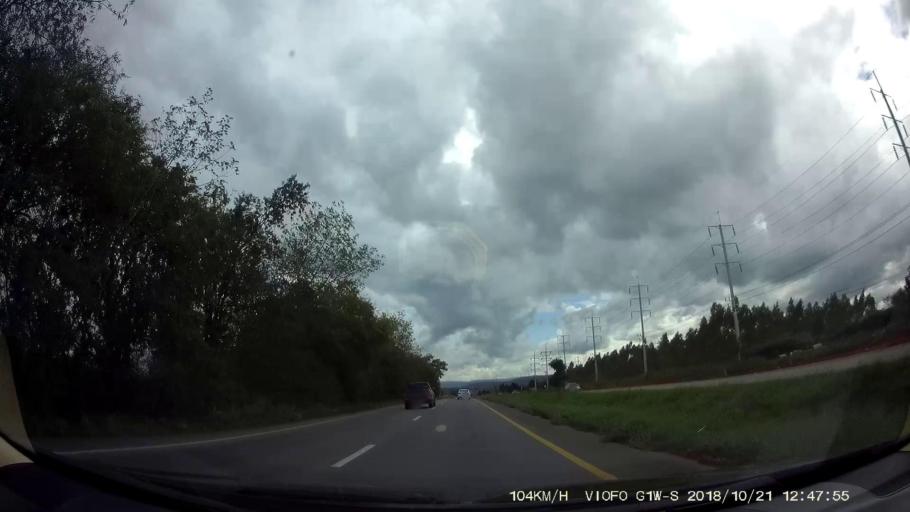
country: TH
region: Nakhon Ratchasima
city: Amphoe Sikhiu
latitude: 14.9209
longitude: 101.6840
